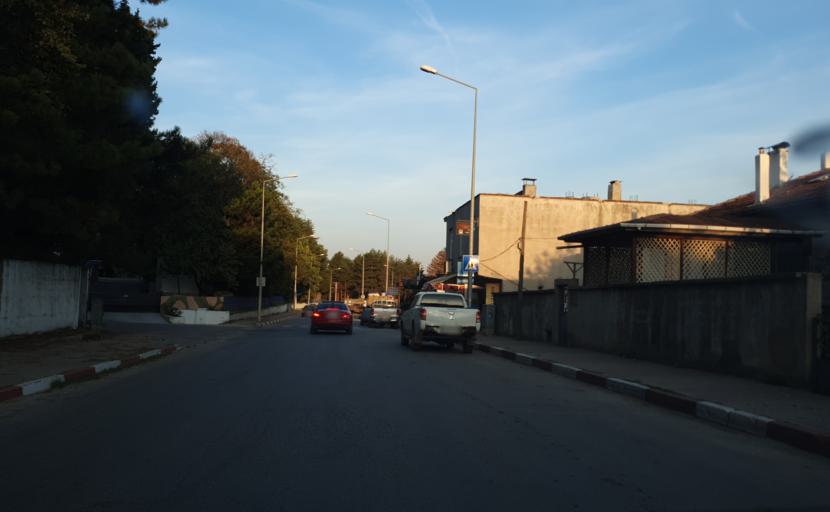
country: TR
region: Kirklareli
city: Sergen
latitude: 41.8240
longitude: 27.7715
